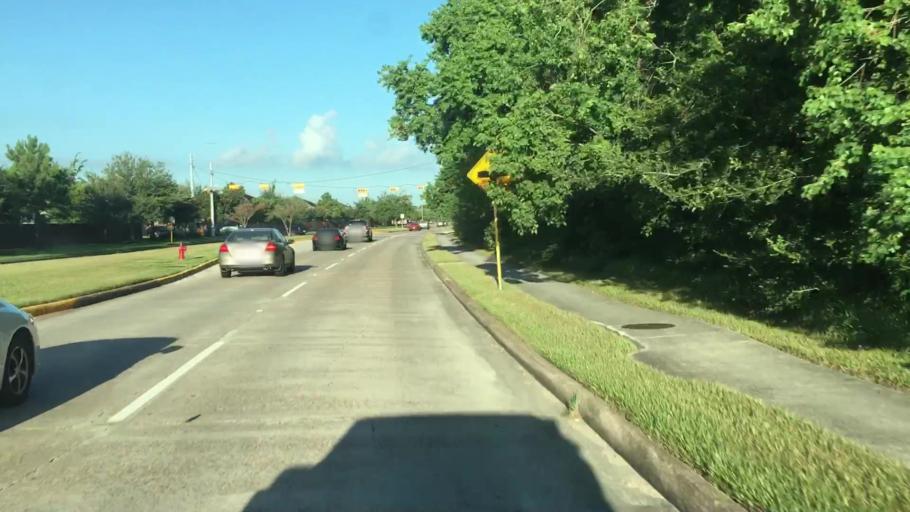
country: US
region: Texas
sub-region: Harris County
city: Atascocita
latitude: 29.9781
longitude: -95.2019
